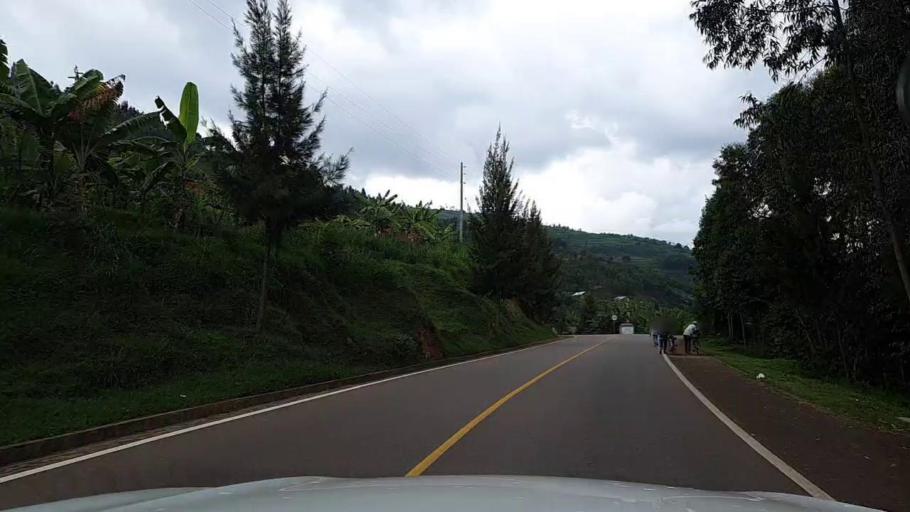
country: RW
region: Northern Province
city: Byumba
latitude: -1.6761
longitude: 30.0957
